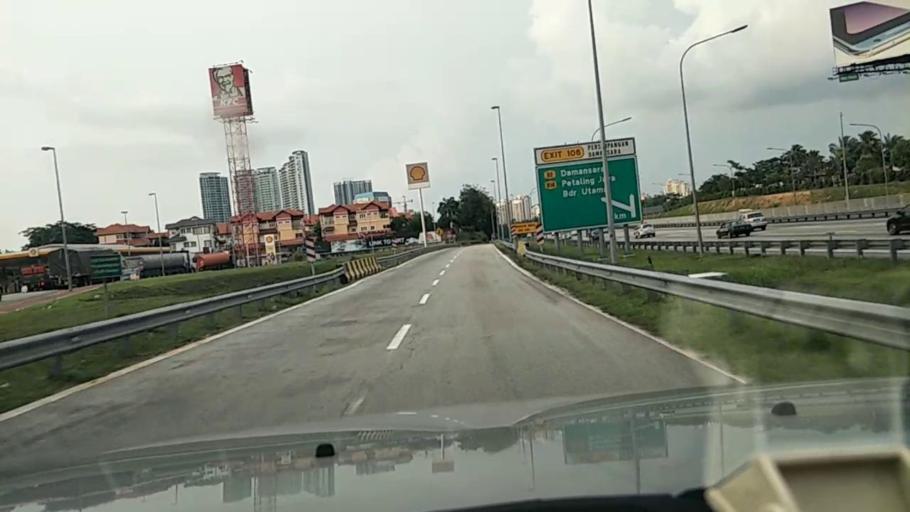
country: MY
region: Selangor
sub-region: Petaling
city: Petaling Jaya
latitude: 3.1216
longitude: 101.5939
